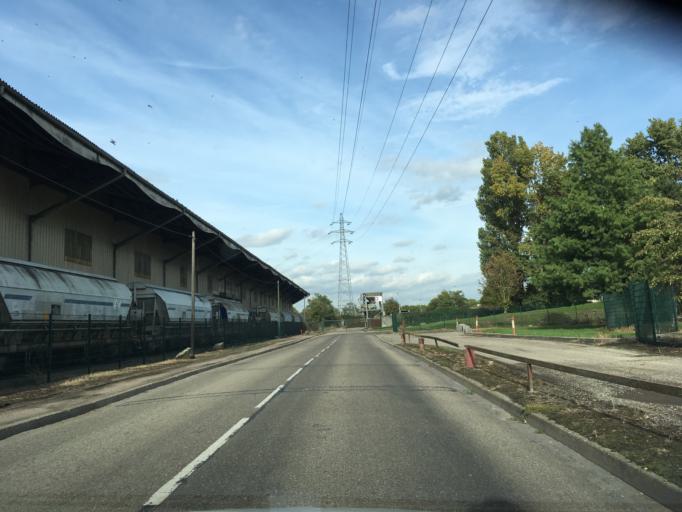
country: DE
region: Baden-Wuerttemberg
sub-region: Freiburg Region
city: Kehl
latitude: 48.5844
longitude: 7.7879
